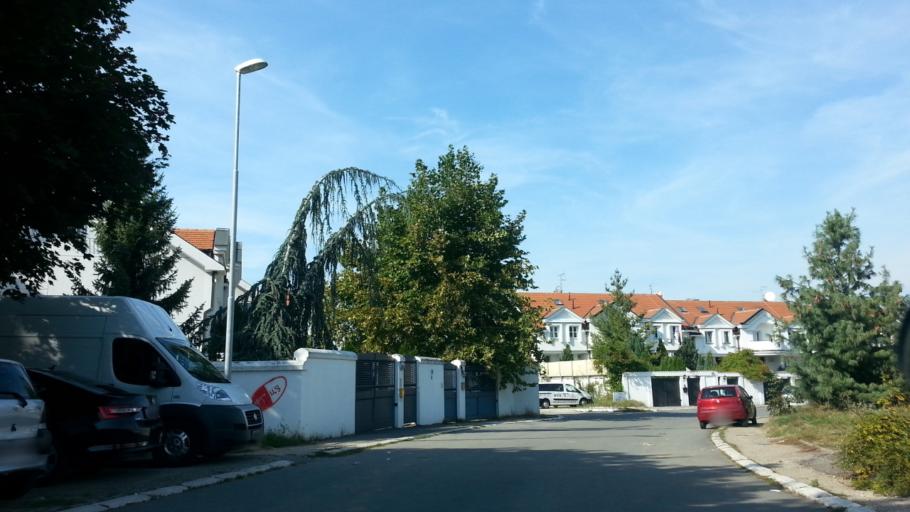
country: RS
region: Central Serbia
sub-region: Belgrade
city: Rakovica
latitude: 44.7506
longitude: 20.4304
